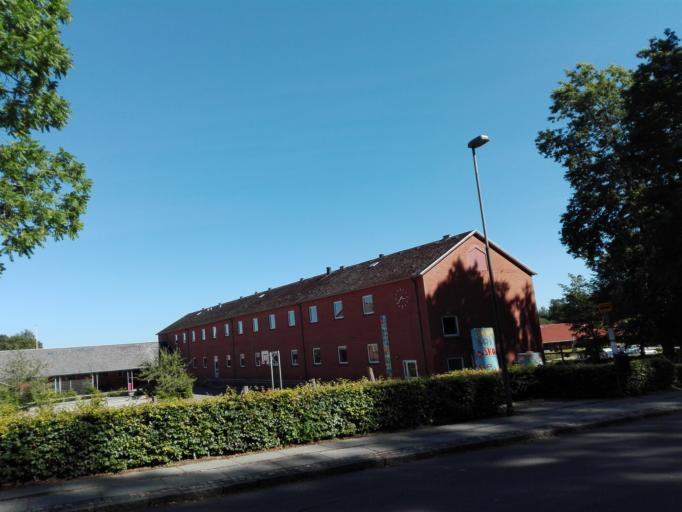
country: DK
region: Central Jutland
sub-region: Odder Kommune
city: Odder
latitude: 55.9693
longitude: 10.1425
